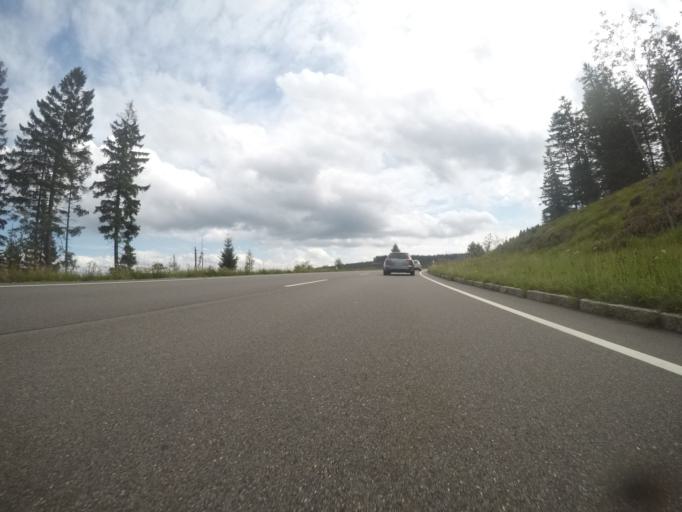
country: DE
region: Baden-Wuerttemberg
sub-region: Freiburg Region
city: Seebach
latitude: 48.5468
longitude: 8.2180
